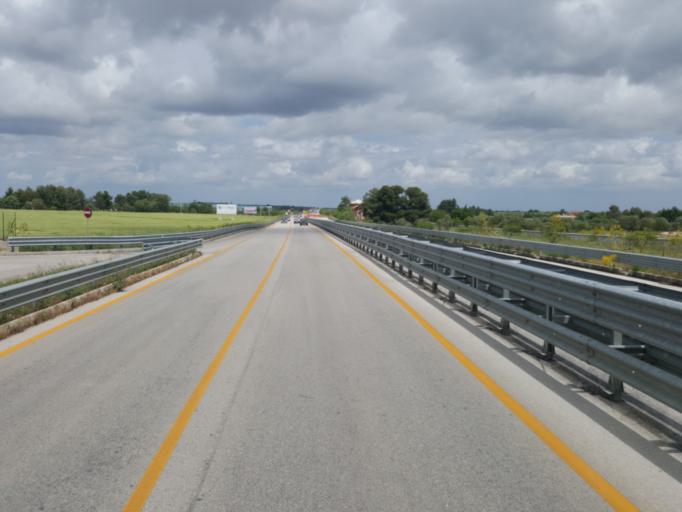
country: IT
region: Apulia
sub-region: Provincia di Bari
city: Toritto
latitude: 40.9417
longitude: 16.6400
